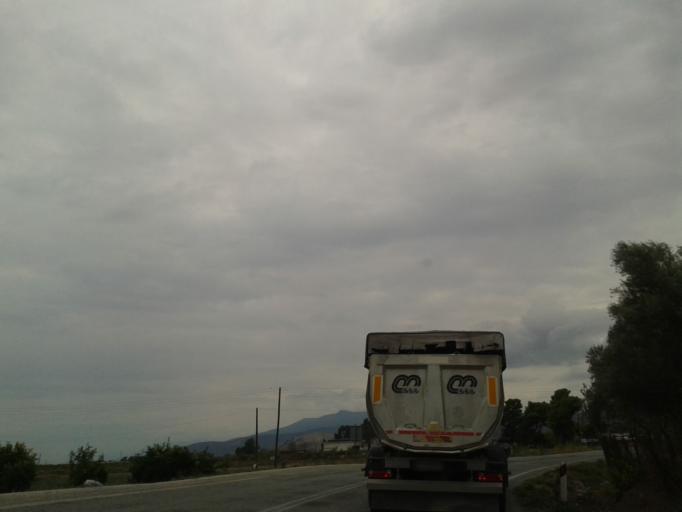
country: GR
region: Peloponnese
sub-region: Nomos Argolidos
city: Nea Kios
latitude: 37.6041
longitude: 22.7090
